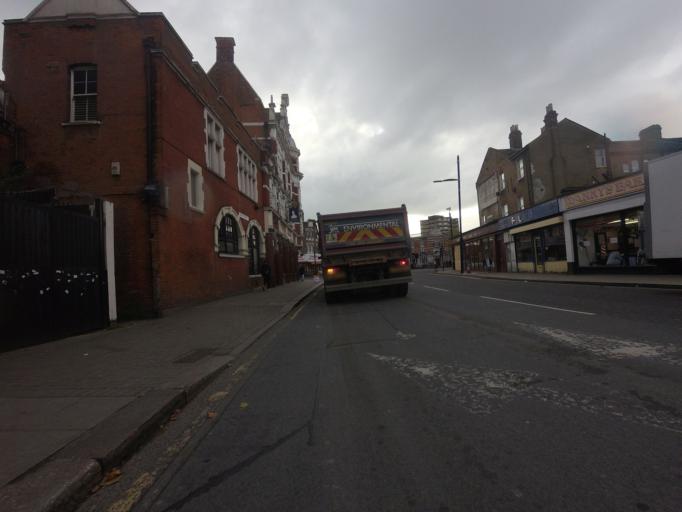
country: GB
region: England
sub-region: Greater London
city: East Ham
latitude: 51.5307
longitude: 0.0379
